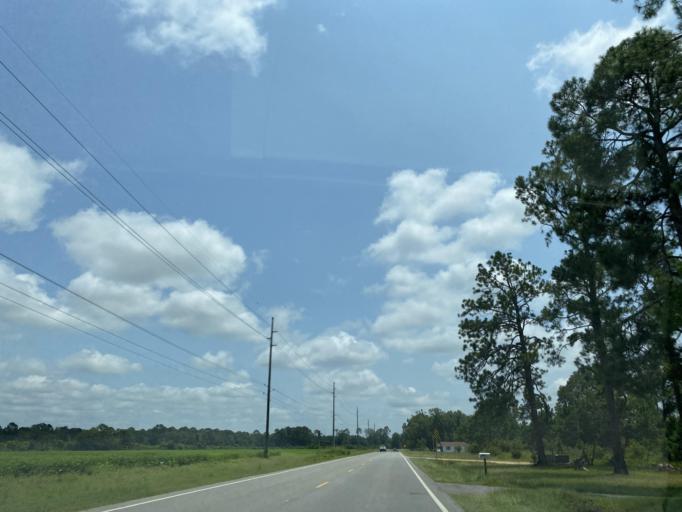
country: US
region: Georgia
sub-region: Jeff Davis County
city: Hazlehurst
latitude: 31.8262
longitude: -82.5718
